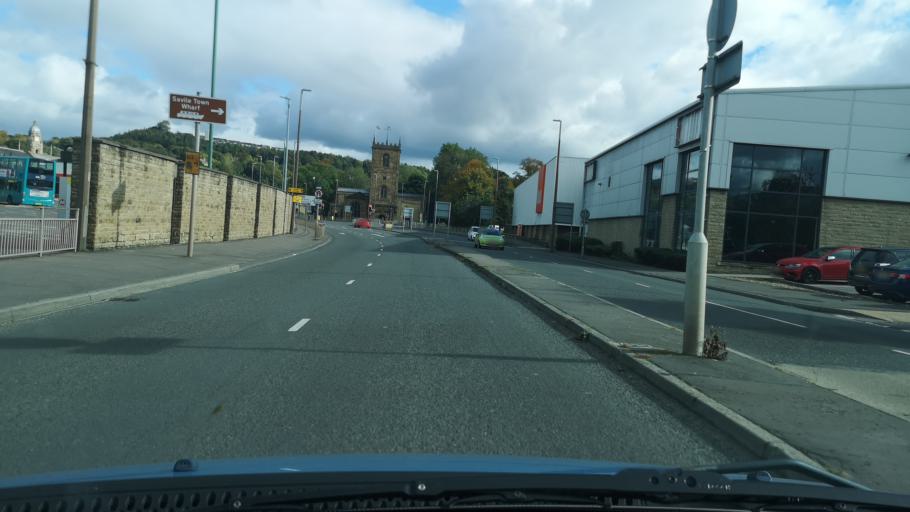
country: GB
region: England
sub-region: Kirklees
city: Dewsbury
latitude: 53.6892
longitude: -1.6324
